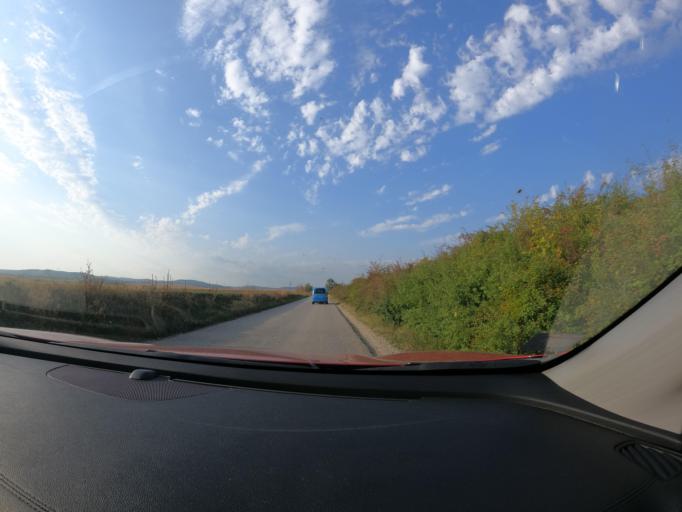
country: RS
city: Vrdnik
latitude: 45.0873
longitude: 19.8066
